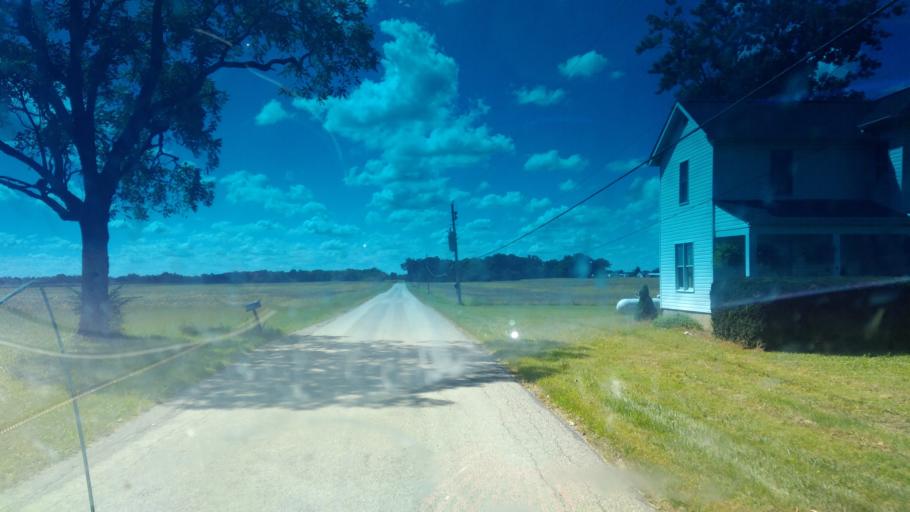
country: US
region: Ohio
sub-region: Madison County
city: West Jefferson
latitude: 39.9845
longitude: -83.3198
